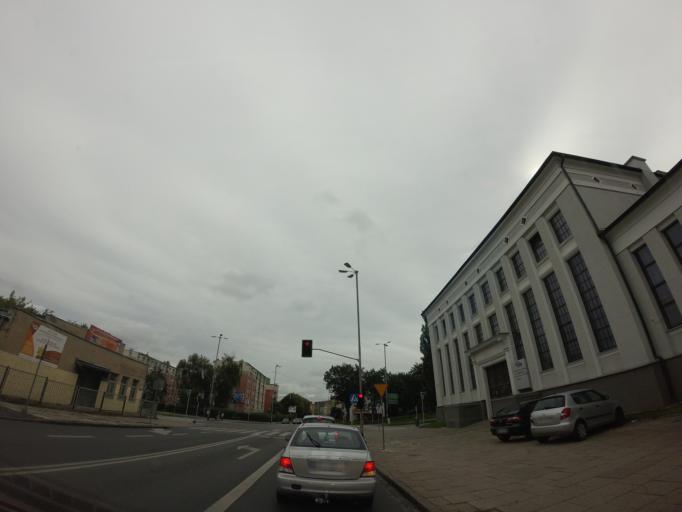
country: PL
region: West Pomeranian Voivodeship
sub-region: Szczecin
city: Szczecin
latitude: 53.4397
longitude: 14.5625
